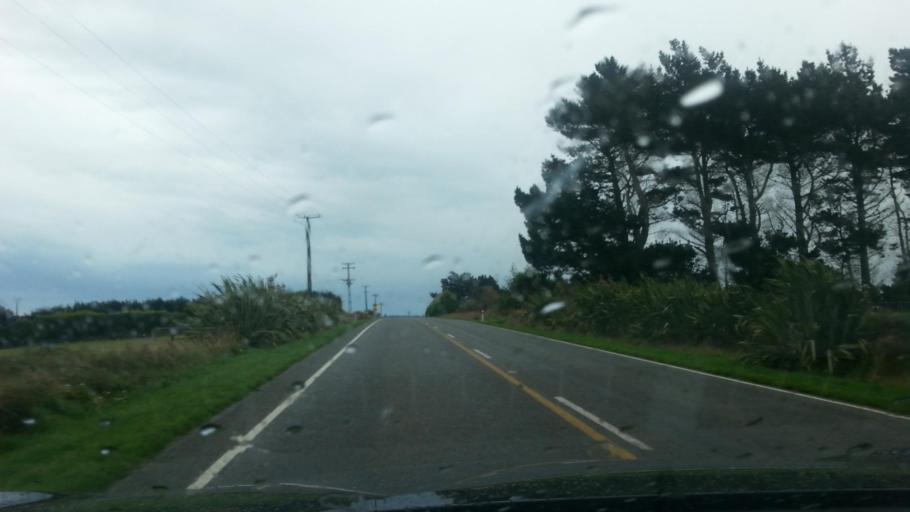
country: NZ
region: Southland
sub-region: Invercargill City
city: Invercargill
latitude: -46.3487
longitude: 168.3885
